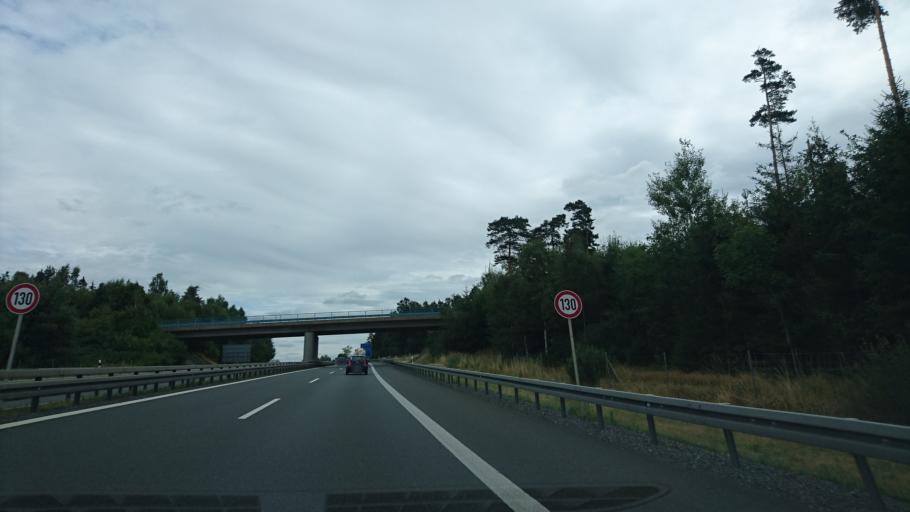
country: DE
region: Bavaria
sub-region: Upper Franconia
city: Thiersheim
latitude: 50.0675
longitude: 12.0991
